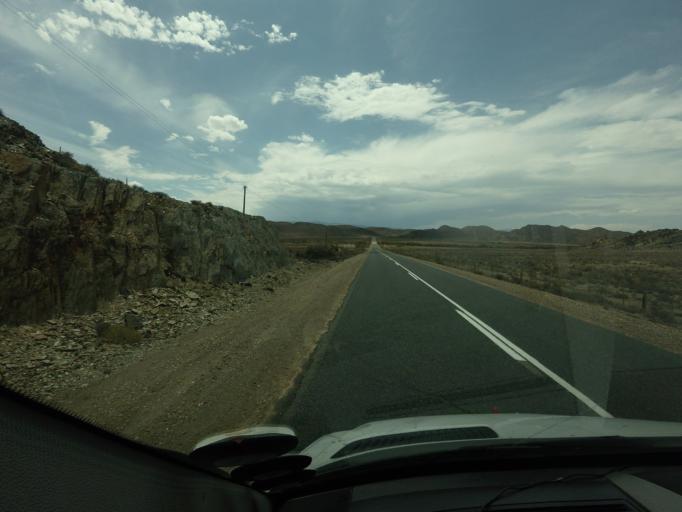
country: ZA
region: Western Cape
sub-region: Eden District Municipality
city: Ladismith
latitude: -33.7334
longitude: 20.9568
